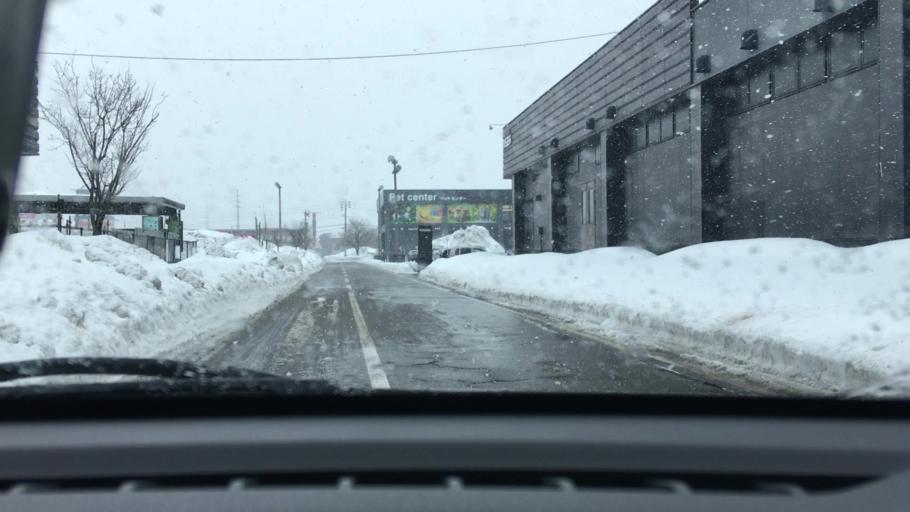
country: JP
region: Niigata
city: Joetsu
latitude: 37.1558
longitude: 138.2530
